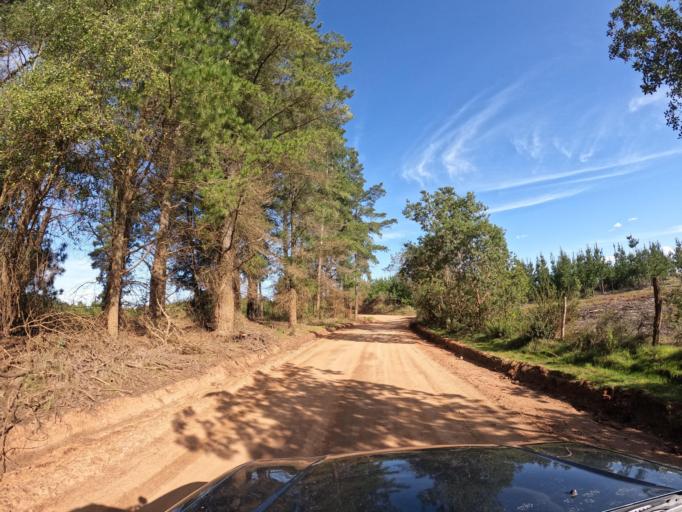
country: CL
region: Biobio
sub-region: Provincia de Biobio
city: La Laja
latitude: -37.1114
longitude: -72.7402
